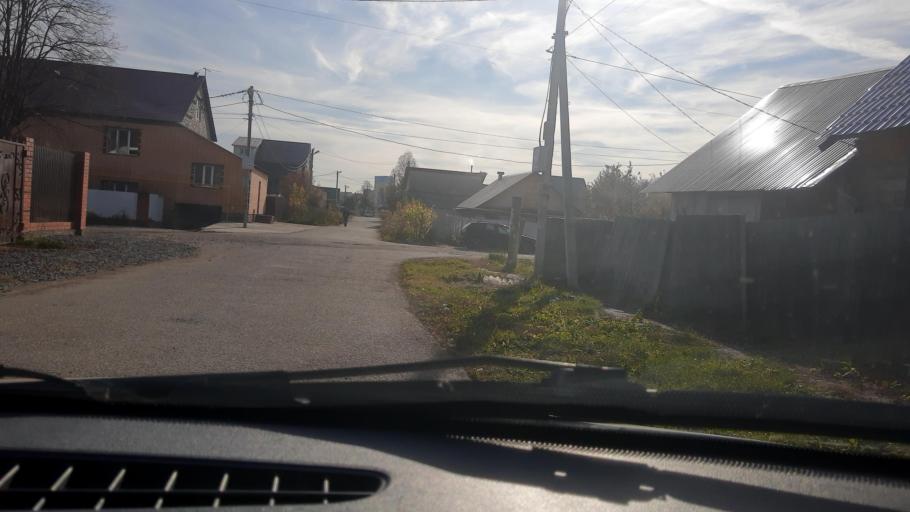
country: RU
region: Bashkortostan
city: Ufa
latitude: 54.7804
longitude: 56.0608
